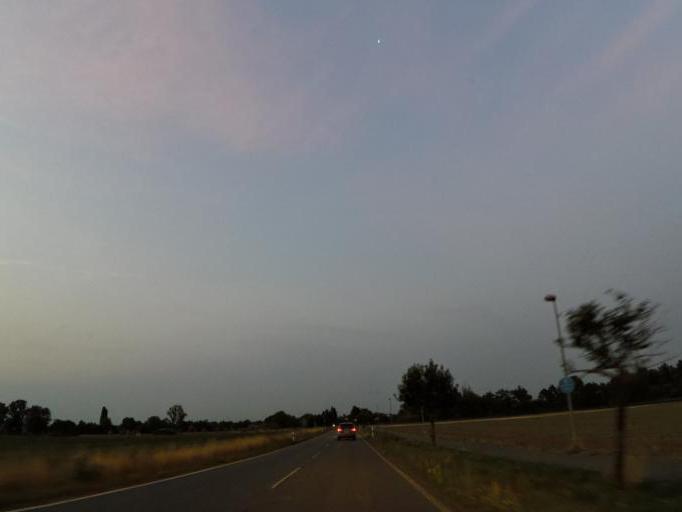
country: DE
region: Hesse
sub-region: Regierungsbezirk Darmstadt
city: Gross-Gerau
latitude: 49.9167
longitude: 8.4649
